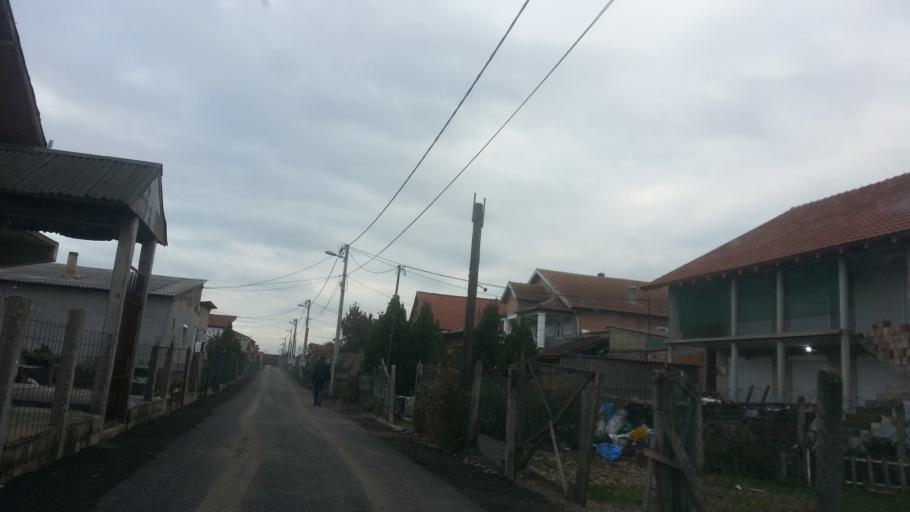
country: RS
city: Novi Banovci
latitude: 44.9193
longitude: 20.2712
